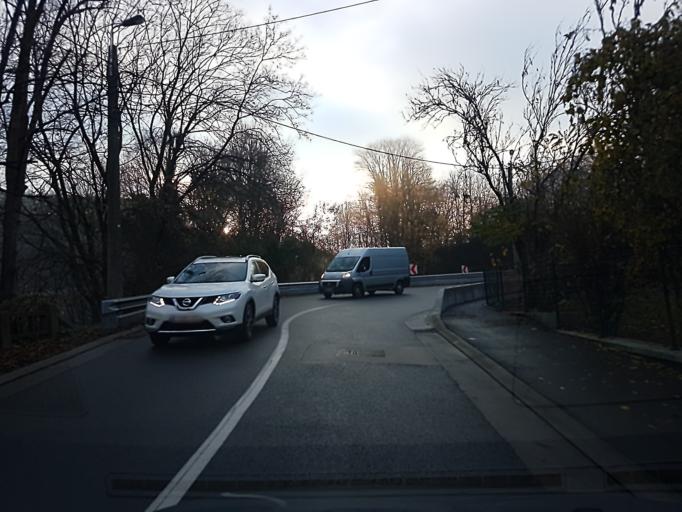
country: BE
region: Wallonia
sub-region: Province de Liege
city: Pepinster
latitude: 50.5608
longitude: 5.8116
